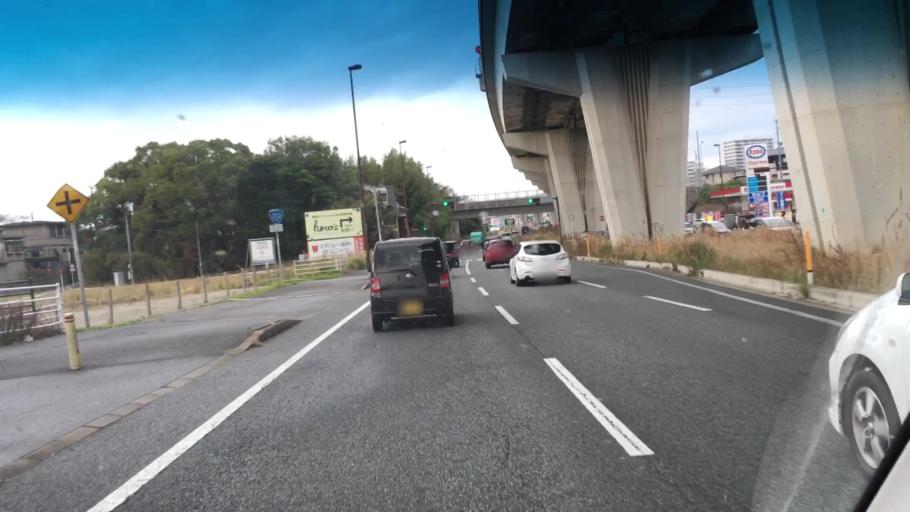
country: JP
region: Fukuoka
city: Maebaru-chuo
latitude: 33.5728
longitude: 130.2683
